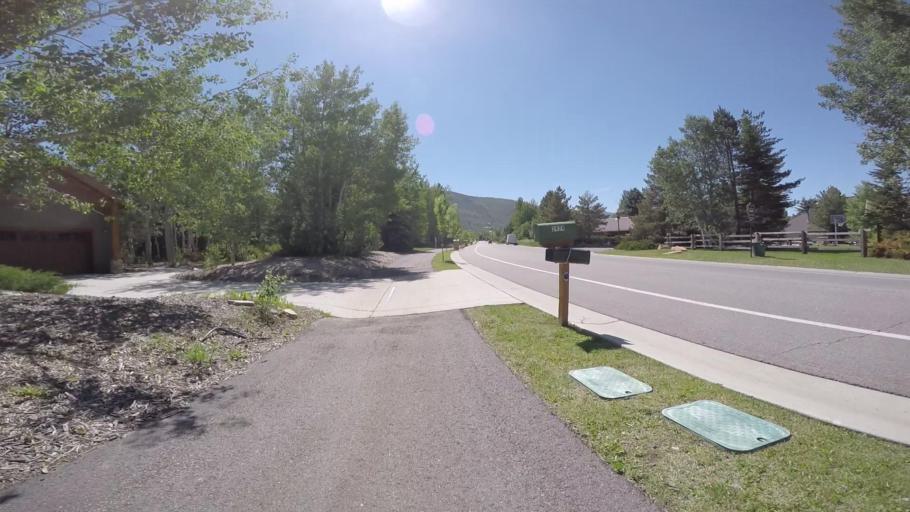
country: US
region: Utah
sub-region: Summit County
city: Park City
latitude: 40.6682
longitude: -111.5091
